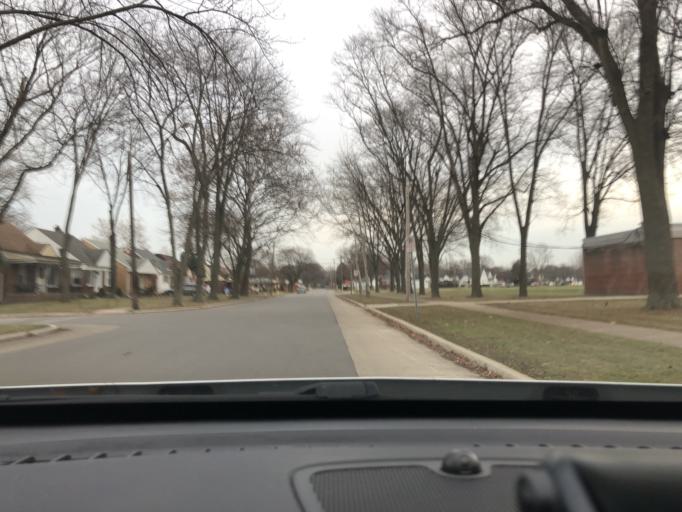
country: US
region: Michigan
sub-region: Wayne County
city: Allen Park
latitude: 42.2845
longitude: -83.2265
